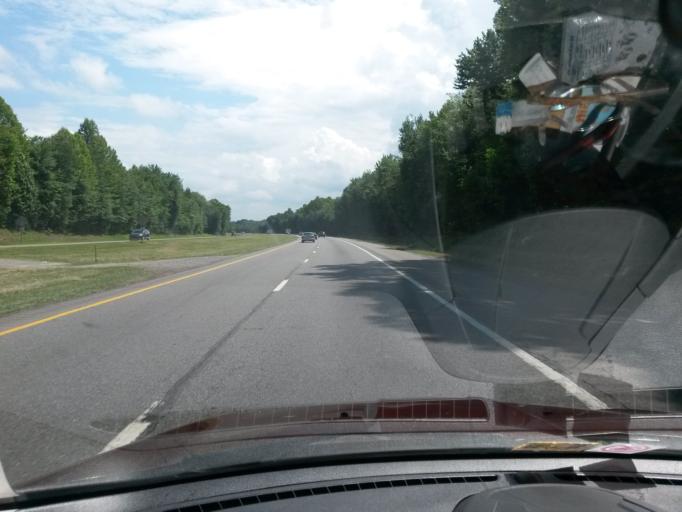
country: US
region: North Carolina
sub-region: Surry County
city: Dobson
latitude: 36.3631
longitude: -80.7982
